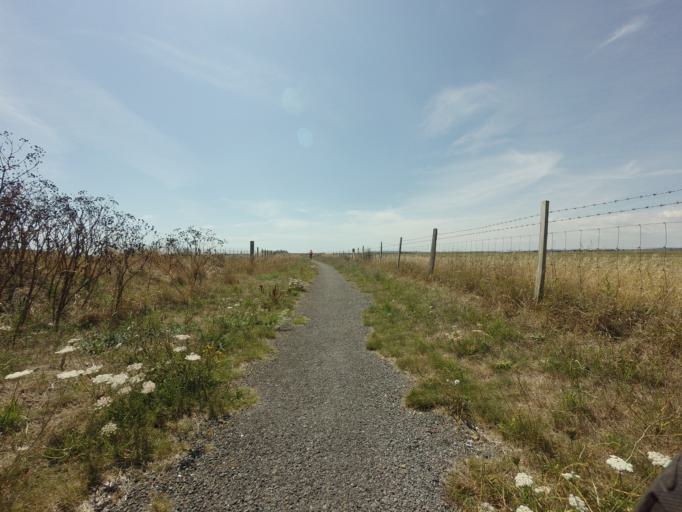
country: GB
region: England
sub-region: Kent
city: Lydd
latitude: 50.9318
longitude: 0.8397
